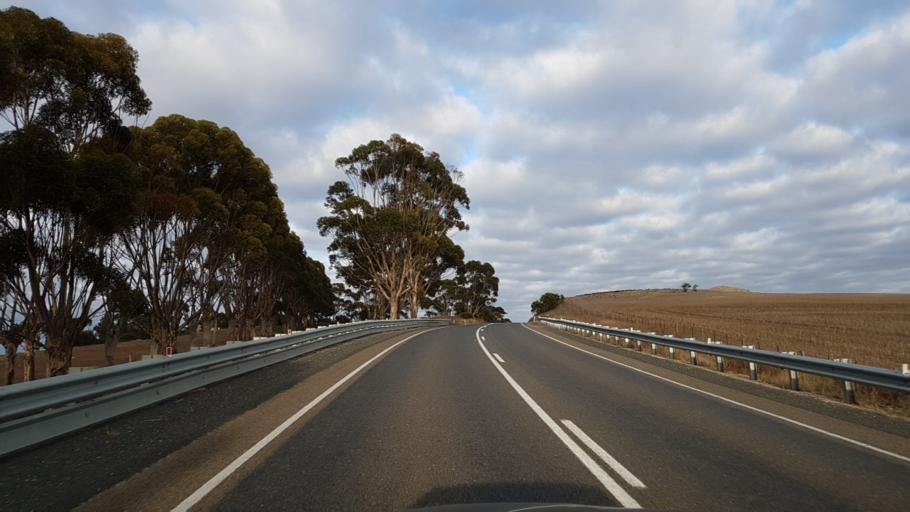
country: AU
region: South Australia
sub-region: Mount Barker
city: Callington
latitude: -35.1787
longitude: 139.0141
